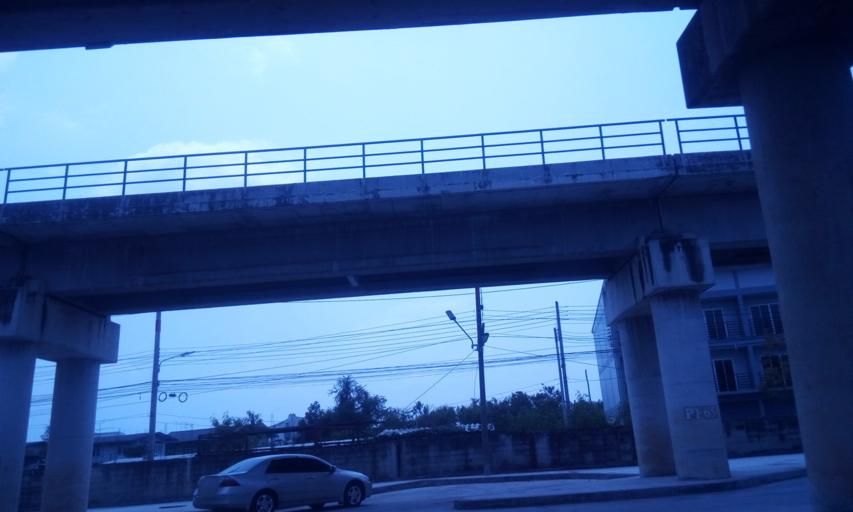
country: TH
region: Chachoengsao
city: Chachoengsao
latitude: 13.6974
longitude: 101.0889
